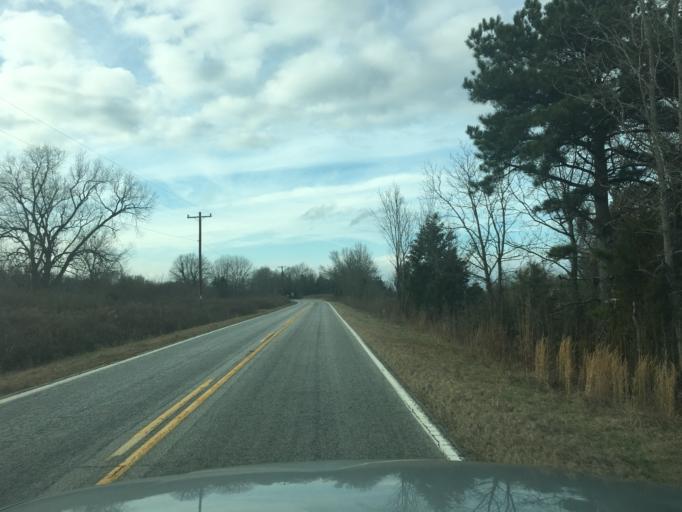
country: US
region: South Carolina
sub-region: Abbeville County
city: Lake Secession
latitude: 34.3559
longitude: -82.5070
